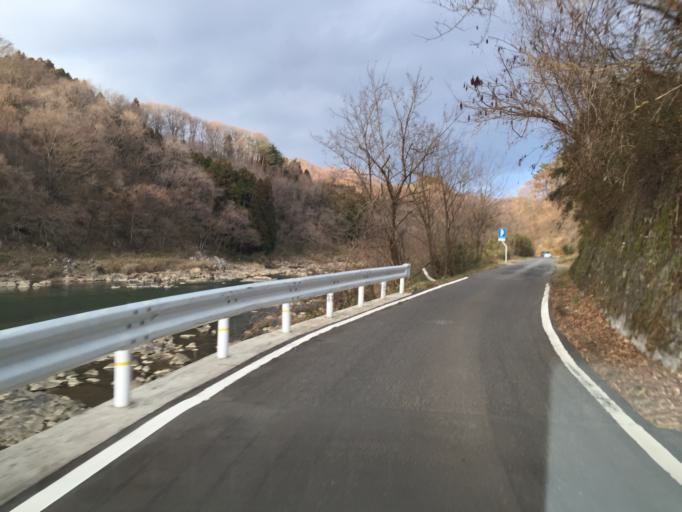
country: JP
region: Fukushima
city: Motomiya
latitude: 37.5354
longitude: 140.4161
